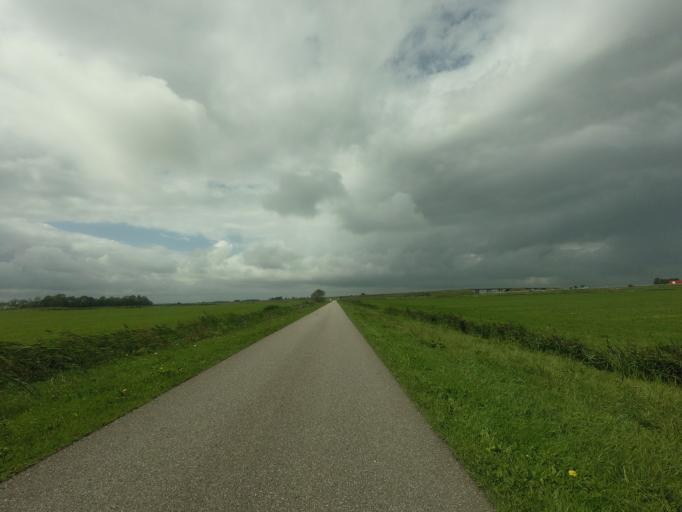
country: NL
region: Friesland
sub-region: Sudwest Fryslan
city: Oppenhuizen
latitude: 52.9831
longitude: 5.7295
